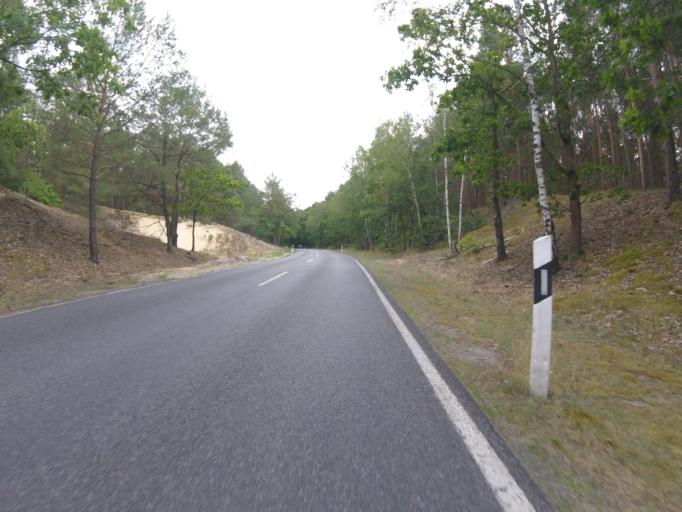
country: DE
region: Brandenburg
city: Halbe
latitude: 52.0982
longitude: 13.7090
